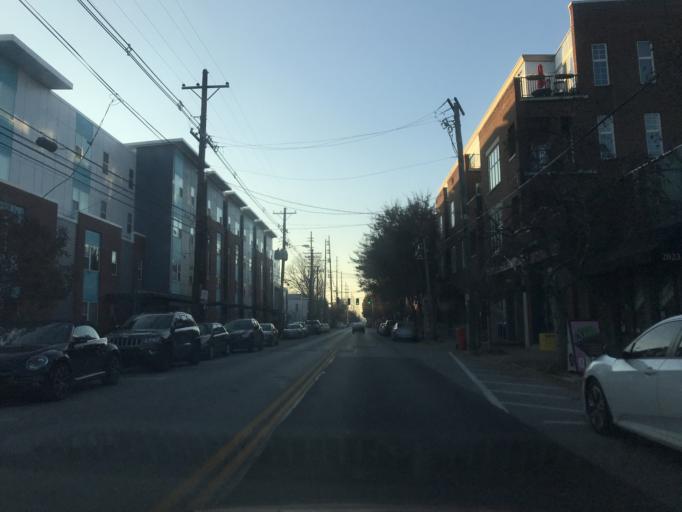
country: US
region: Indiana
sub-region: Clark County
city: Jeffersonville
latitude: 38.2539
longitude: -85.7078
